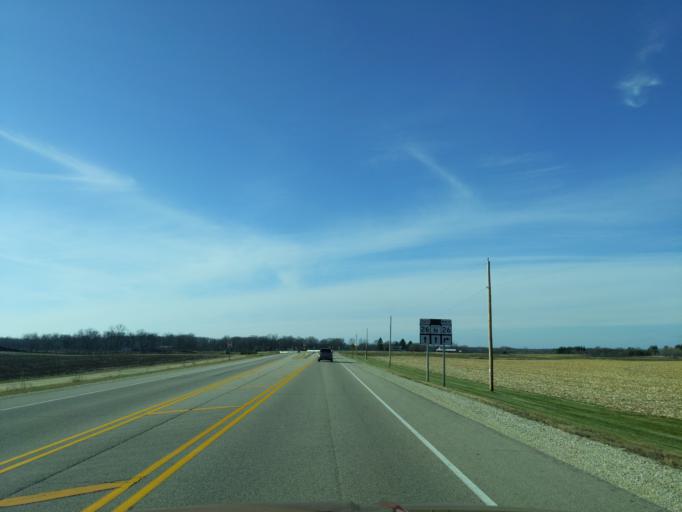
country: US
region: Wisconsin
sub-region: Rock County
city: Milton
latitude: 42.8231
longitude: -88.9208
